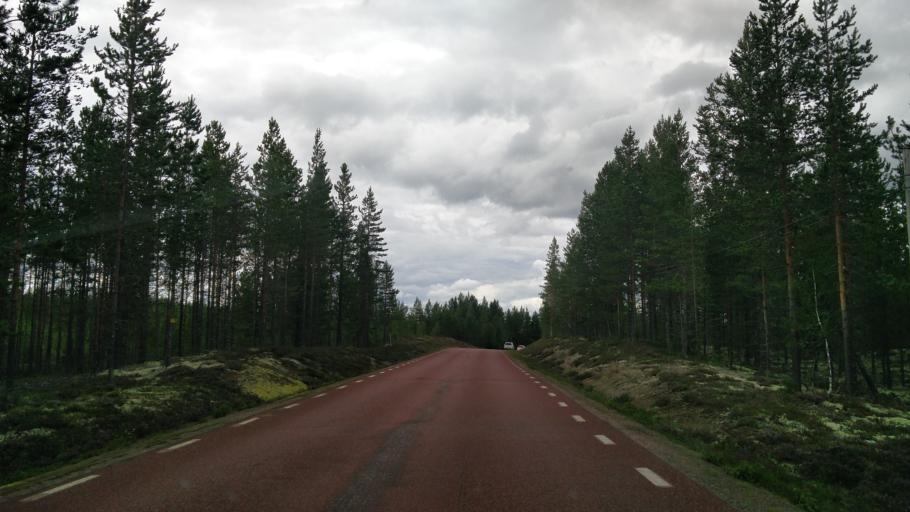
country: NO
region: Hedmark
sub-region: Trysil
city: Innbygda
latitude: 61.1456
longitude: 12.8050
